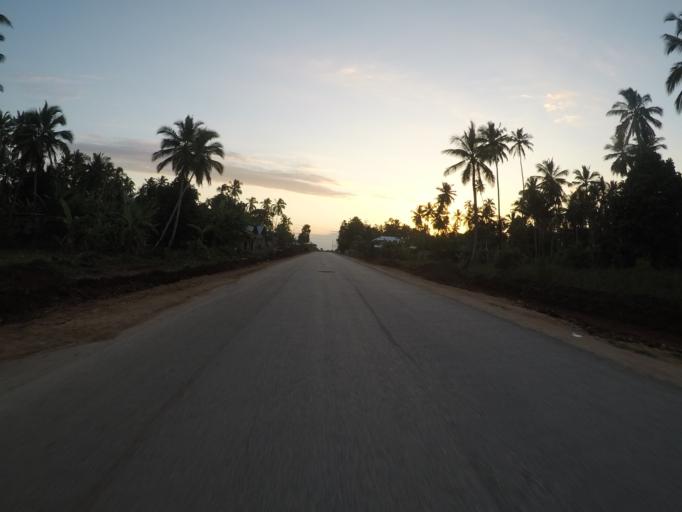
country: TZ
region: Zanzibar North
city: Gamba
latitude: -5.9877
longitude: 39.2645
